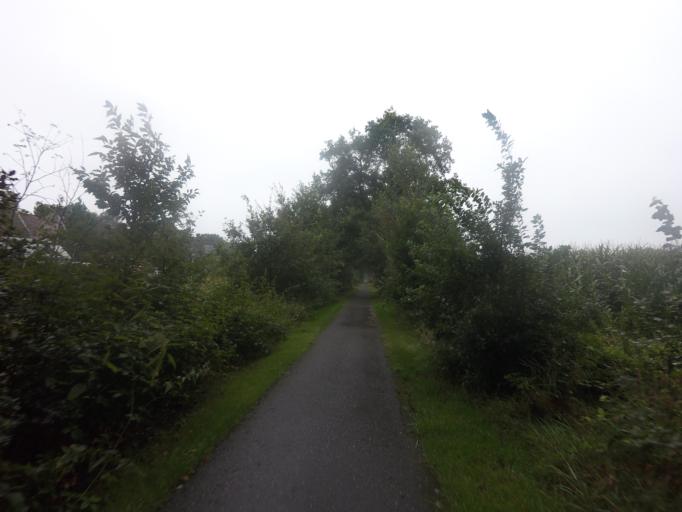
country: NL
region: Friesland
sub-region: Gemeente Heerenveen
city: Nieuwehorne
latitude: 52.9512
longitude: 6.0543
